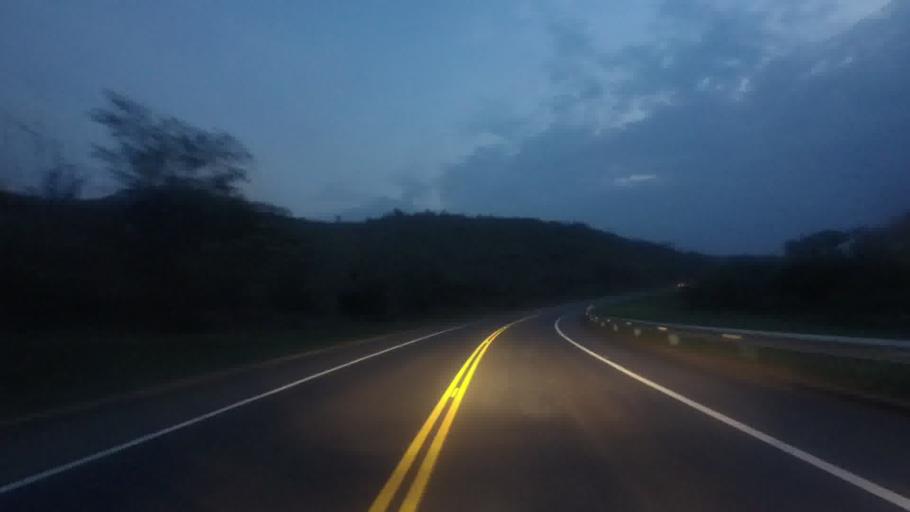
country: BR
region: Rio de Janeiro
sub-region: Sapucaia
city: Sapucaia
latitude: -21.9458
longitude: -42.8341
